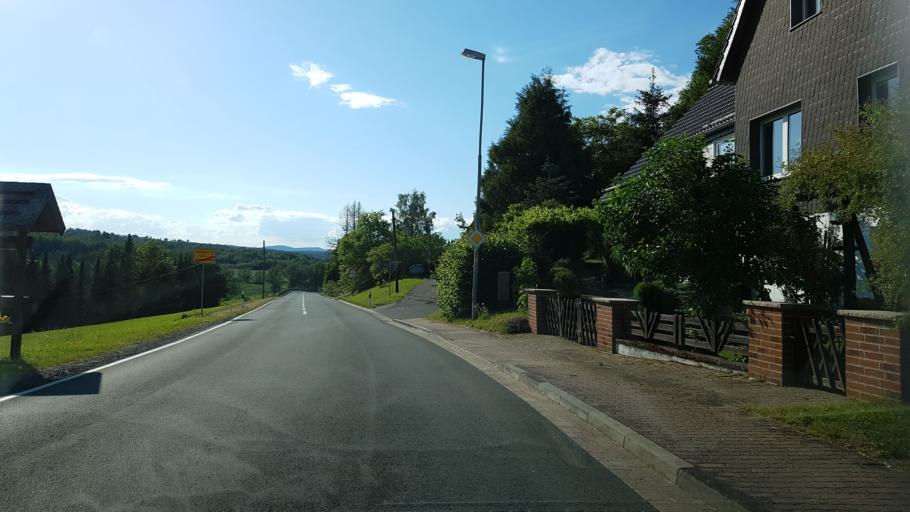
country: DE
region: Lower Saxony
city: Coppengrave
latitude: 51.9713
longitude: 9.7628
